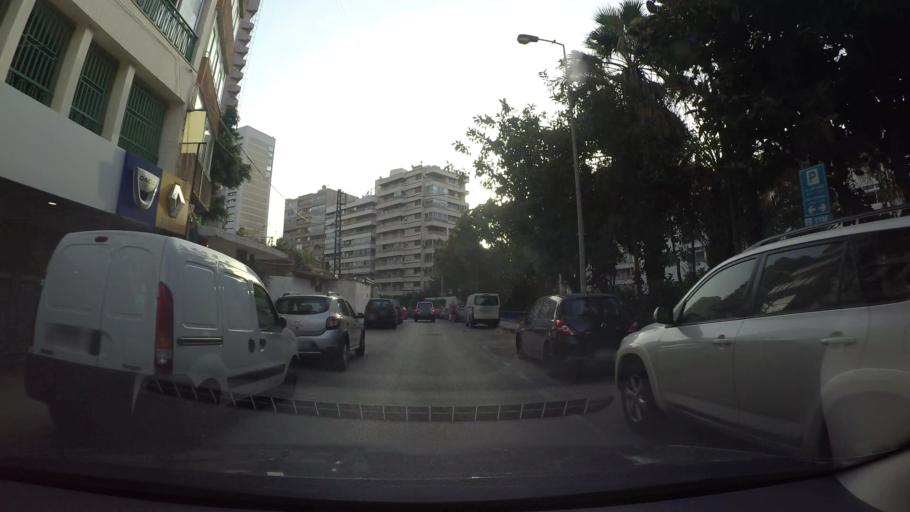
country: LB
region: Beyrouth
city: Ra's Bayrut
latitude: 33.8939
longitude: 35.4758
